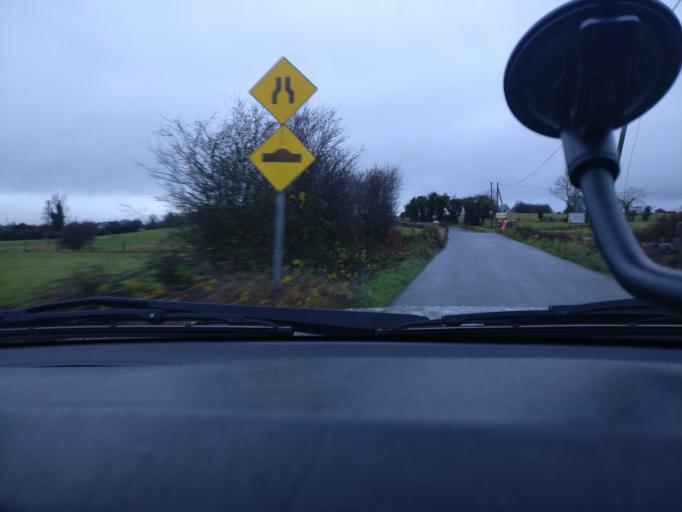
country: IE
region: Connaught
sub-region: County Galway
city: Loughrea
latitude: 53.2580
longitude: -8.5857
